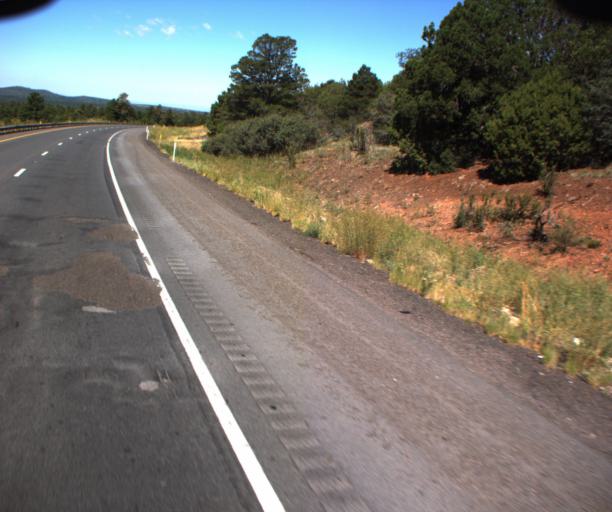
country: US
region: Arizona
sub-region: Coconino County
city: Williams
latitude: 35.2243
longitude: -112.2417
